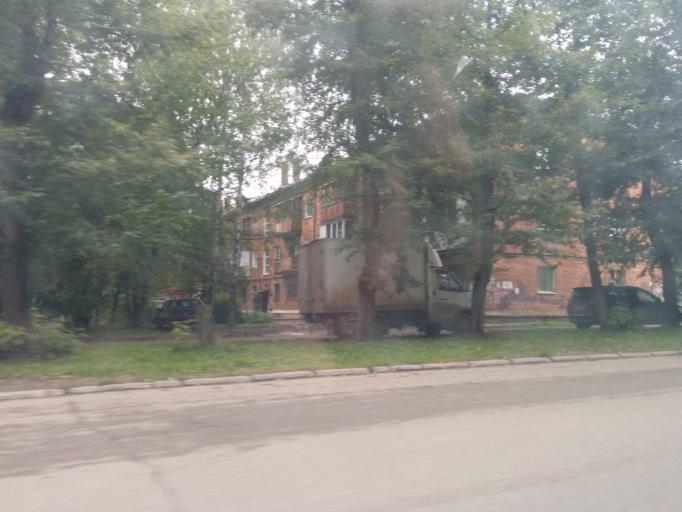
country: RU
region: Perm
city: Perm
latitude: 57.9988
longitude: 56.3015
